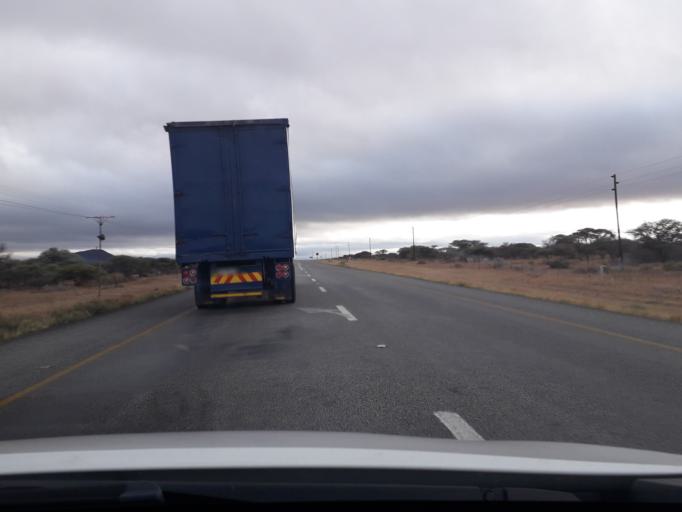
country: ZA
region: Limpopo
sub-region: Capricorn District Municipality
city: Polokwane
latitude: -23.7361
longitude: 29.5780
